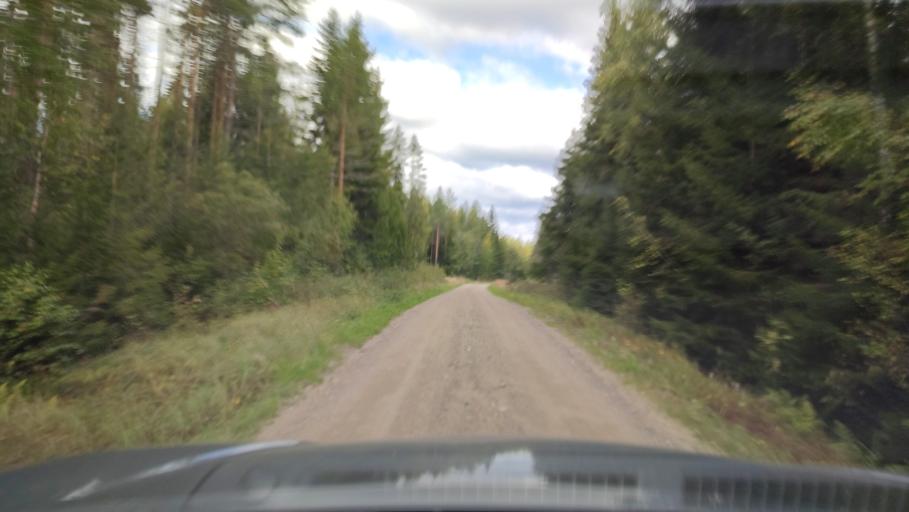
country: FI
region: Southern Ostrobothnia
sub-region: Suupohja
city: Karijoki
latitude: 62.2068
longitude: 21.6152
